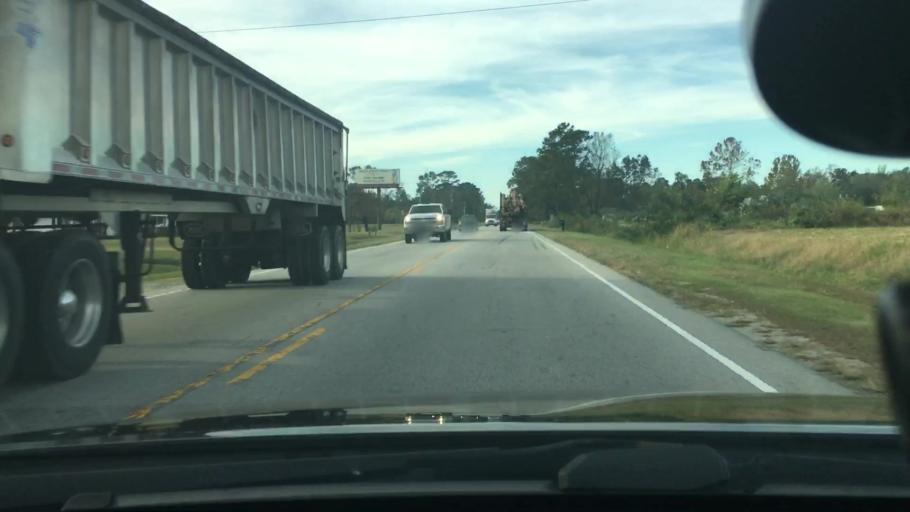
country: US
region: North Carolina
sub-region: Craven County
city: Vanceboro
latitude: 35.2707
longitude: -77.1119
